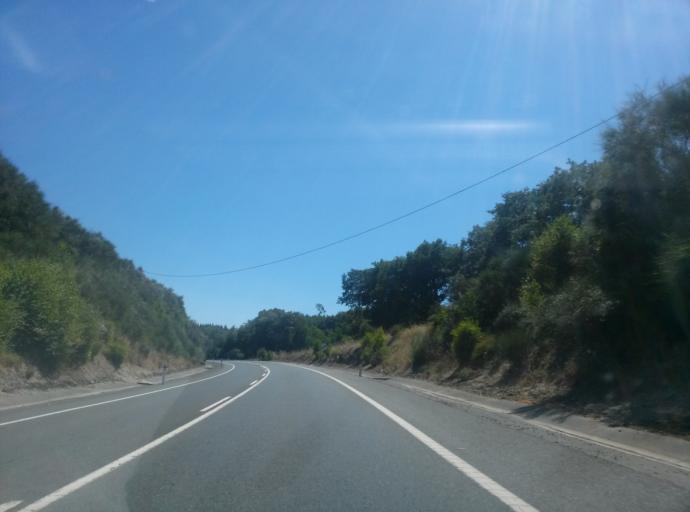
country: ES
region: Galicia
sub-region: Provincia de Lugo
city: Mos
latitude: 43.0936
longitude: -7.4779
